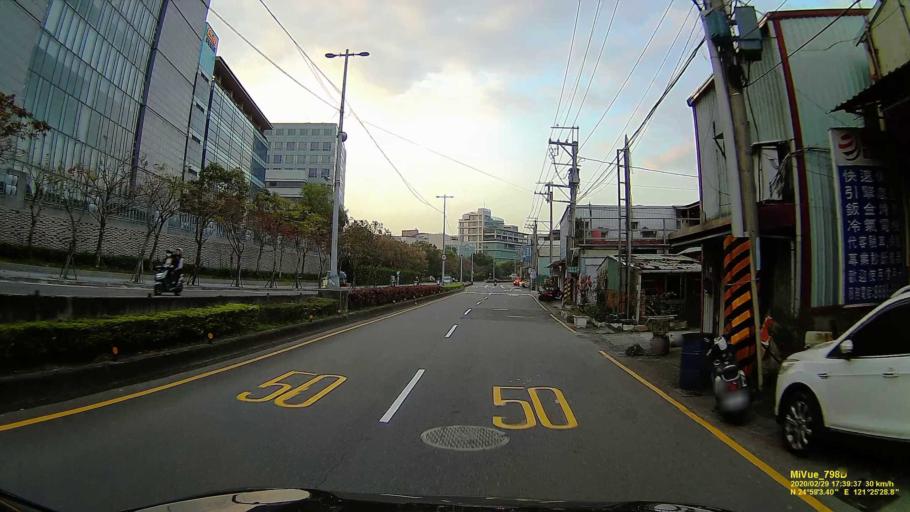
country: TW
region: Taipei
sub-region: Taipei
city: Banqiao
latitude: 24.9845
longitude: 121.4246
